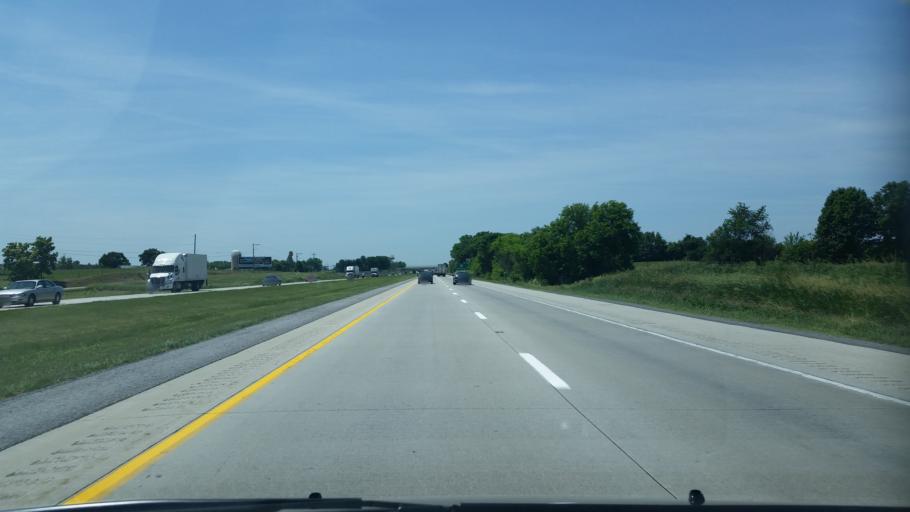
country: US
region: Pennsylvania
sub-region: Franklin County
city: Scotland
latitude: 39.9717
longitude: -77.5739
